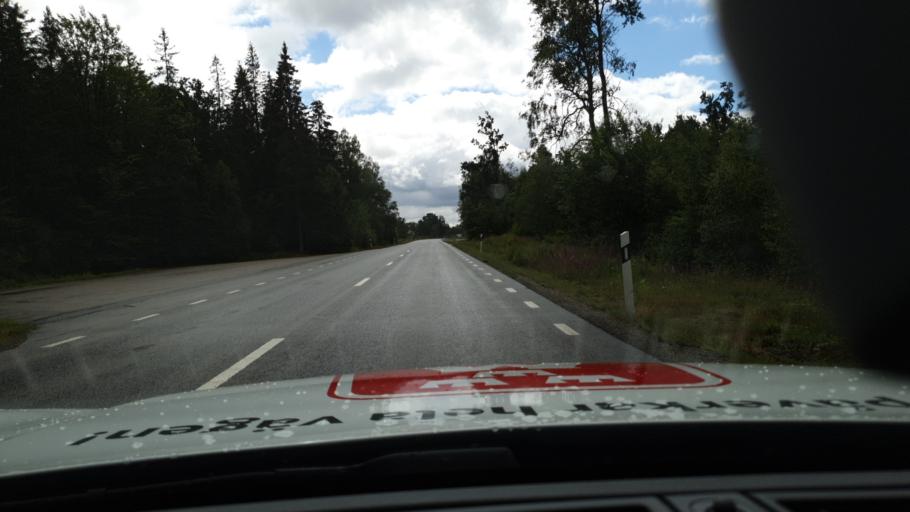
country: SE
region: Kronoberg
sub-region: Vaxjo Kommun
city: Lammhult
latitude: 57.1182
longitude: 14.6322
